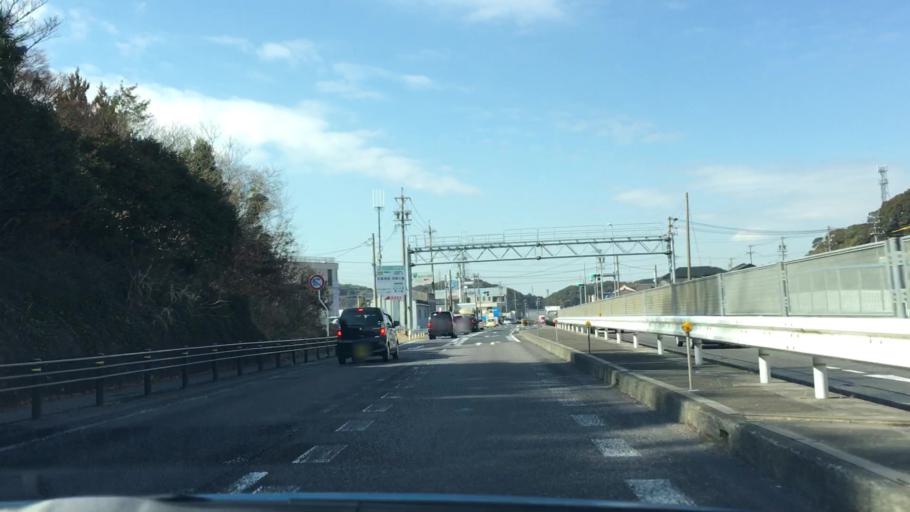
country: JP
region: Aichi
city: Gamagori
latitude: 34.8987
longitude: 137.2430
